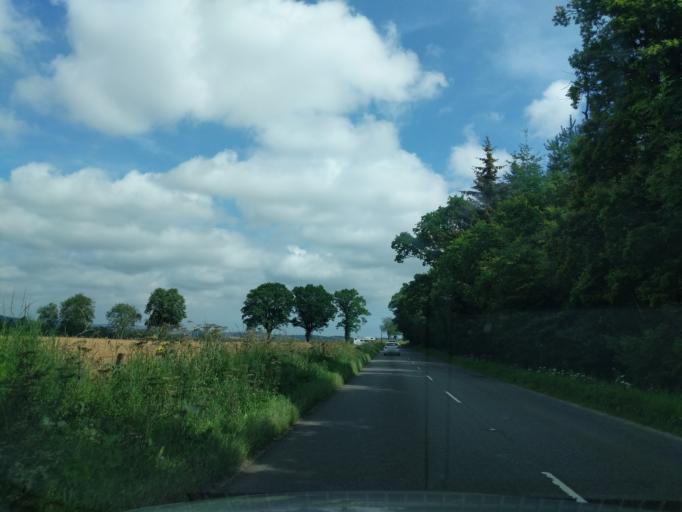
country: GB
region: Scotland
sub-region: Angus
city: Muirhead
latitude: 56.5044
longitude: -3.1265
